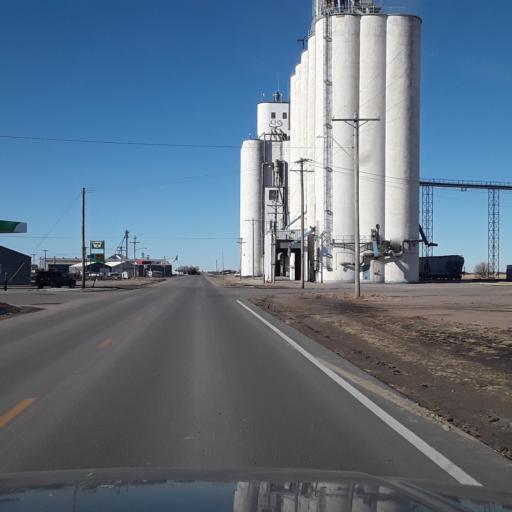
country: US
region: Nebraska
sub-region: Gosper County
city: Elwood
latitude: 40.5279
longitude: -99.6331
